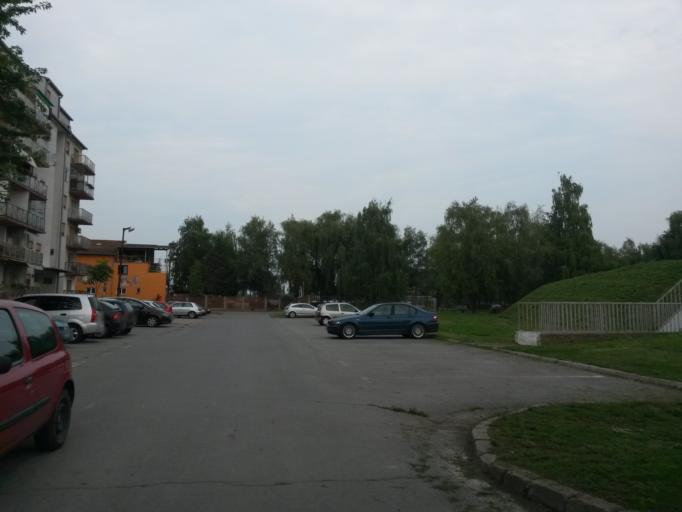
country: HR
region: Osjecko-Baranjska
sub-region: Grad Osijek
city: Osijek
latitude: 45.5445
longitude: 18.7281
